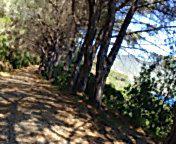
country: IT
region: Tuscany
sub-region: Provincia di Livorno
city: Capoliveri
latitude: 42.7487
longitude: 10.3193
